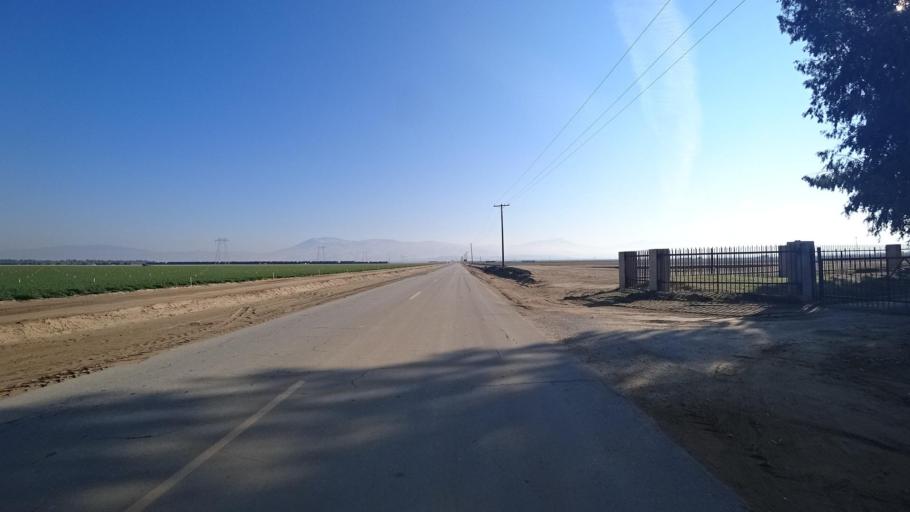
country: US
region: California
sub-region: Kern County
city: Weedpatch
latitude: 35.1220
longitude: -118.9231
